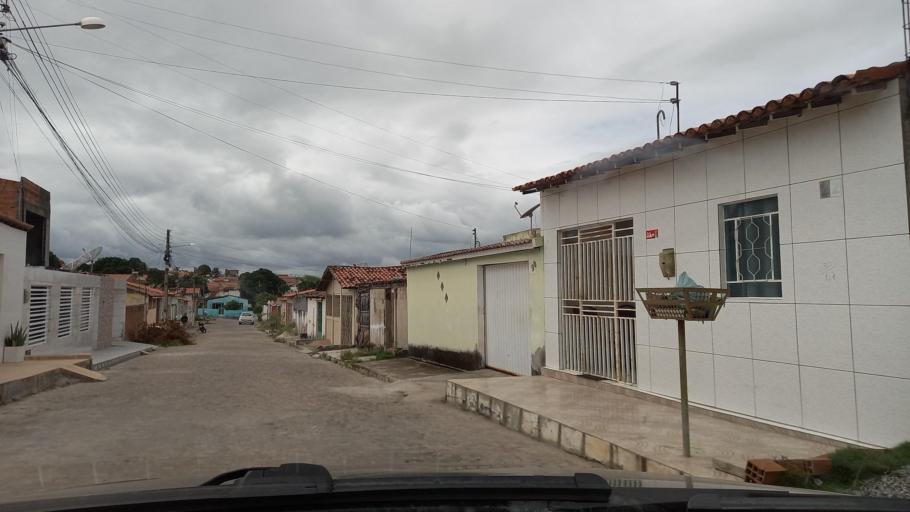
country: BR
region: Sergipe
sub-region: Caninde De Sao Francisco
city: Caninde de Sao Francisco
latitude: -9.6070
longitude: -37.7609
